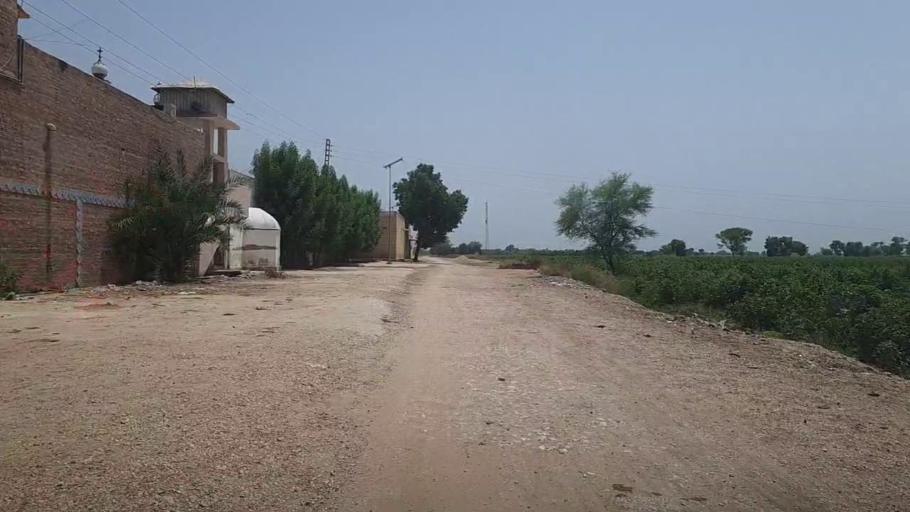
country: PK
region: Sindh
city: Pad Idan
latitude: 26.8435
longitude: 68.3247
